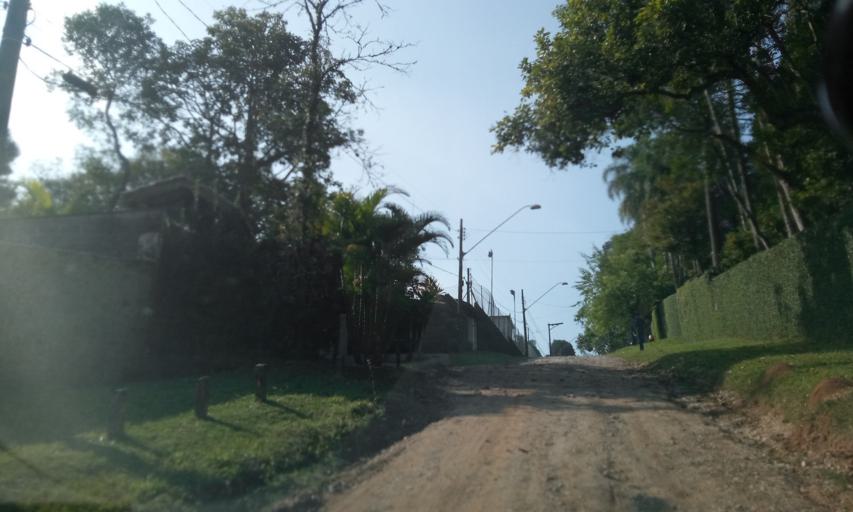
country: BR
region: Sao Paulo
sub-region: Sao Bernardo Do Campo
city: Sao Bernardo do Campo
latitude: -23.7916
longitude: -46.5416
